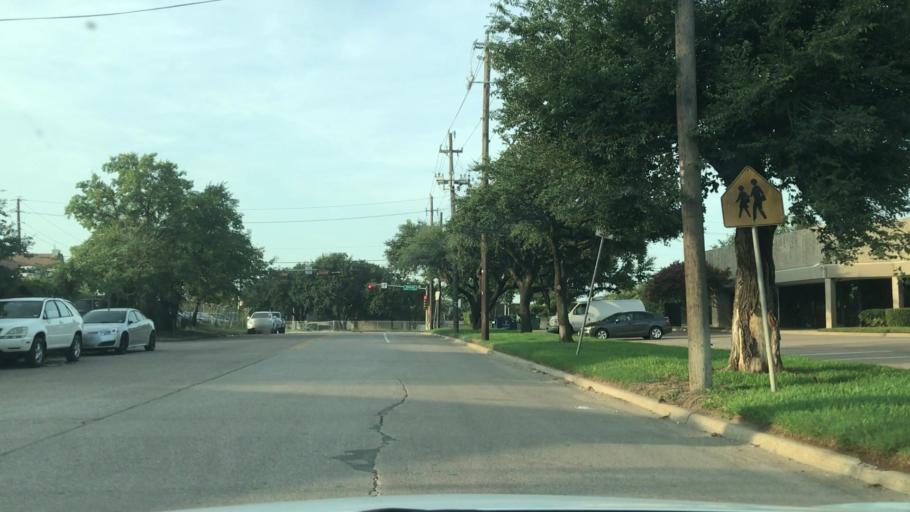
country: US
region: Texas
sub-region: Dallas County
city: Farmers Branch
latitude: 32.8966
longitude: -96.9080
